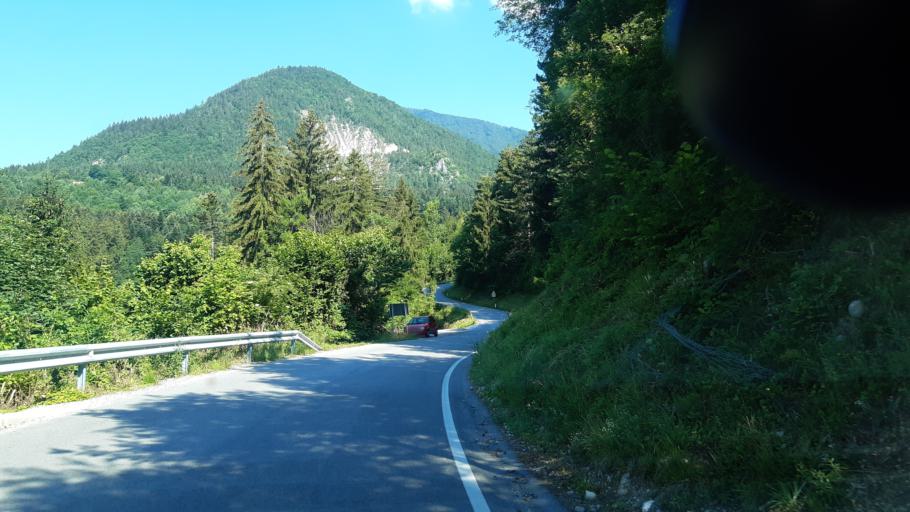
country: SI
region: Trzic
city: Bistrica pri Trzicu
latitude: 46.3561
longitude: 14.2887
